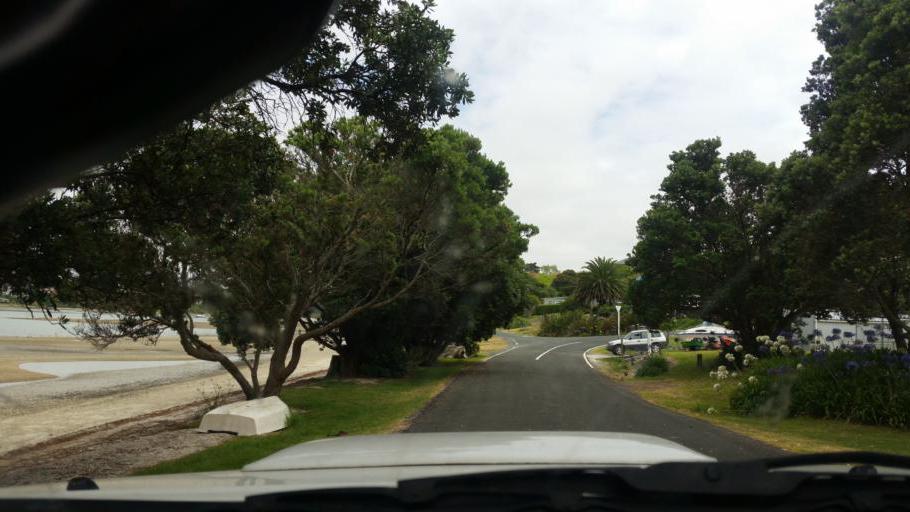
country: NZ
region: Auckland
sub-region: Auckland
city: Wellsford
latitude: -36.1584
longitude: 174.2371
